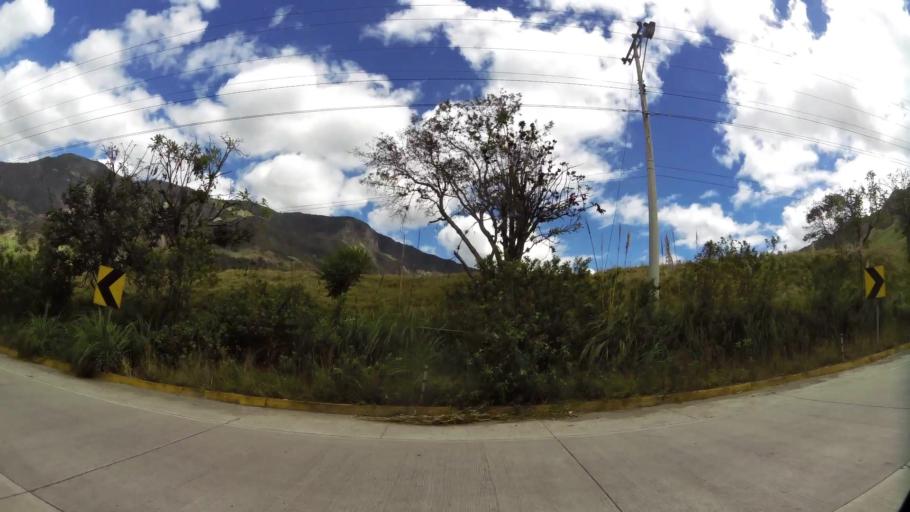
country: EC
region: Azuay
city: Cuenca
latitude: -3.1338
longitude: -79.1219
